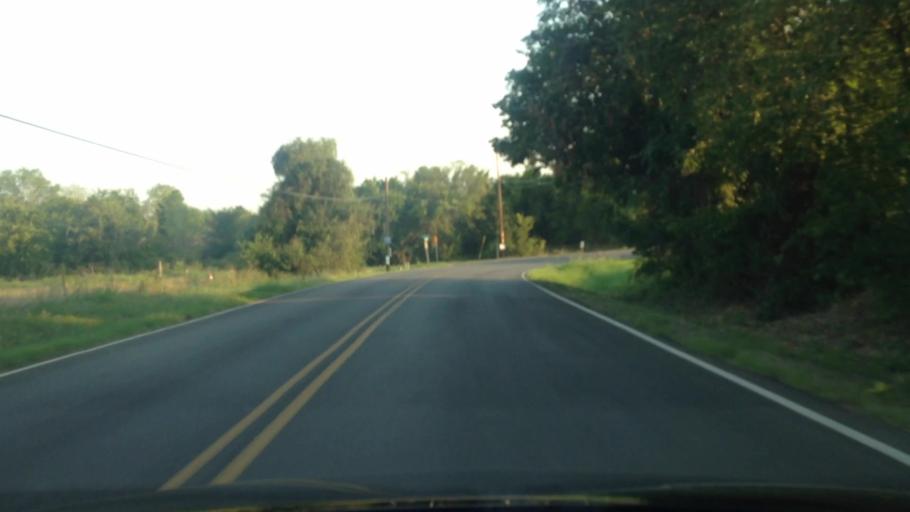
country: US
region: Texas
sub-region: Tarrant County
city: Rendon
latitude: 32.5995
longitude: -97.2153
